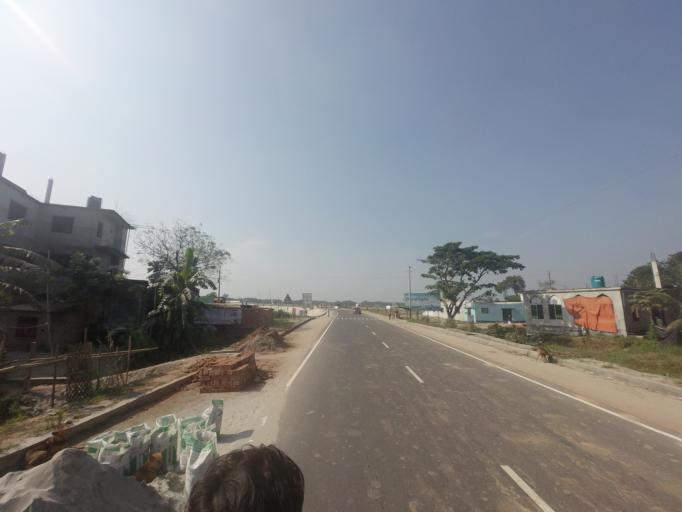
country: BD
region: Dhaka
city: Azimpur
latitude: 23.7350
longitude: 90.3299
